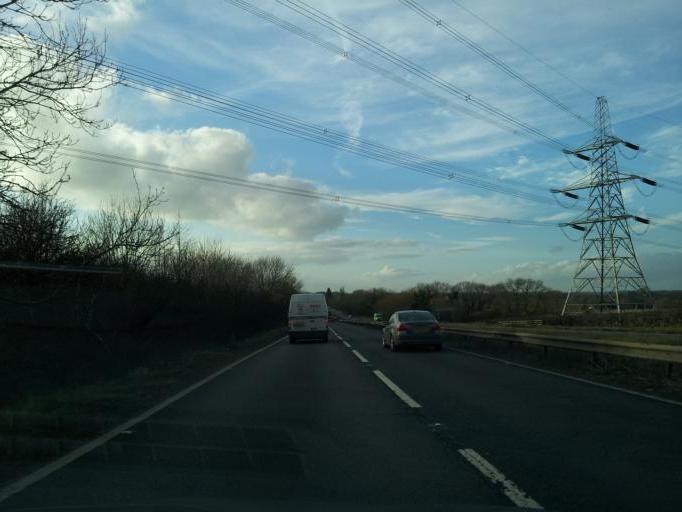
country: GB
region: England
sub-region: Peterborough
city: Upton
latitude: 52.5612
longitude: -0.3747
